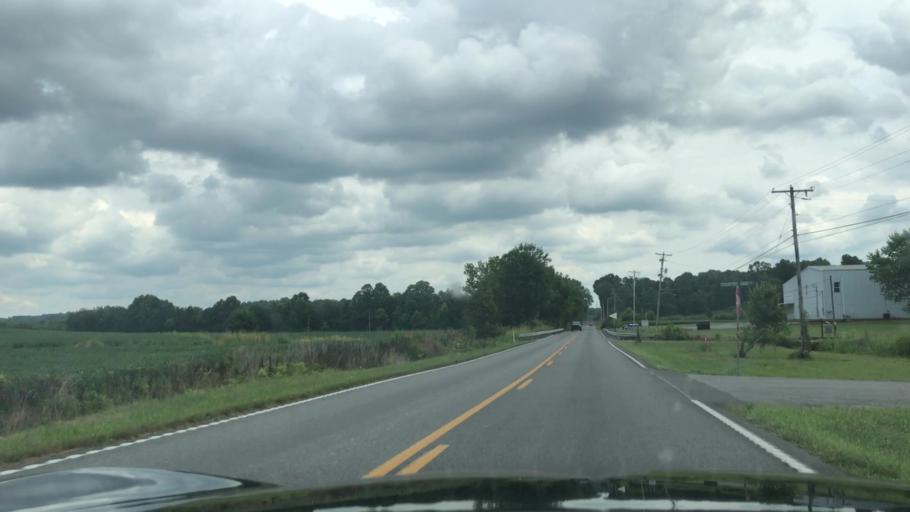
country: US
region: Kentucky
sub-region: Muhlenberg County
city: Greenville
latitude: 37.1975
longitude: -87.1254
